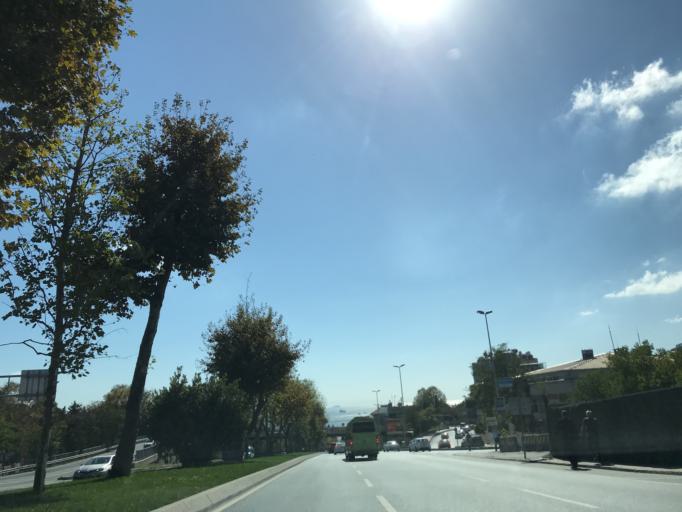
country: TR
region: Istanbul
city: Sisli
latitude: 41.0530
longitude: 29.0091
